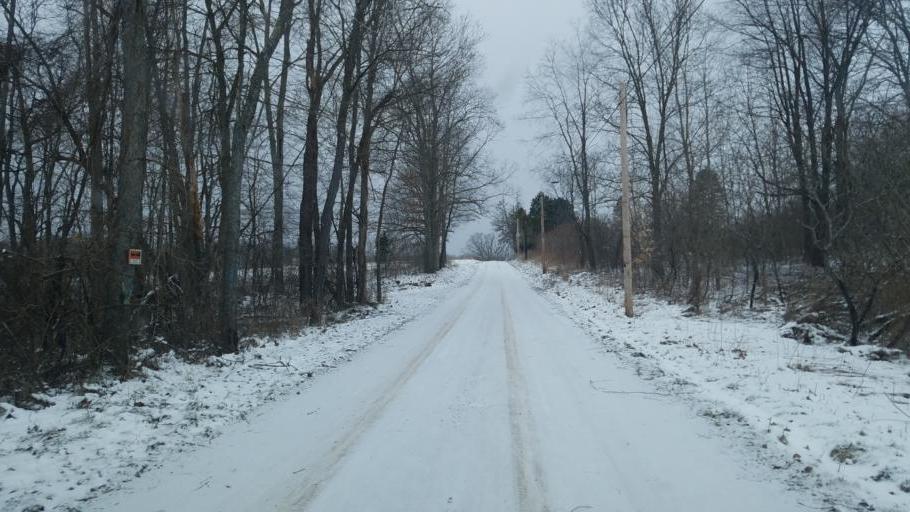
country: US
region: Pennsylvania
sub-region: Crawford County
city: Cochranton
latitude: 41.4630
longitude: -79.9749
